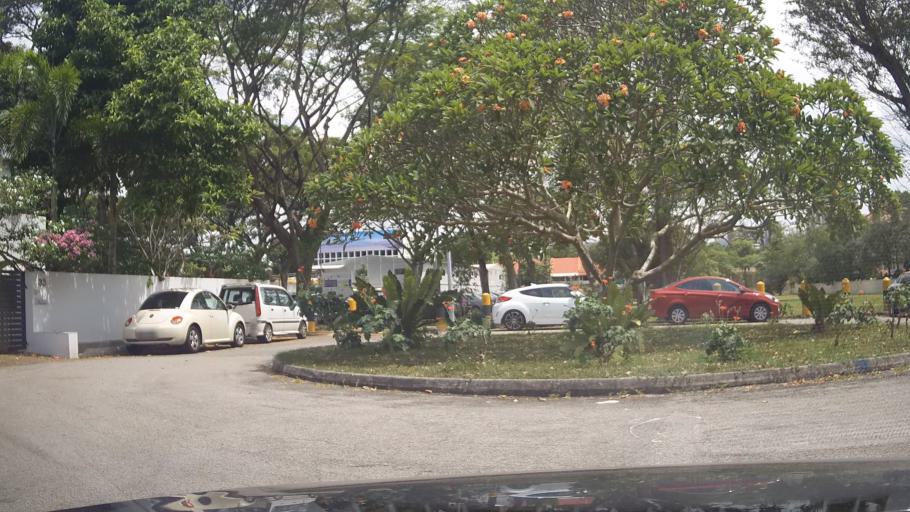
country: SG
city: Singapore
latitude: 1.3117
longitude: 103.9255
